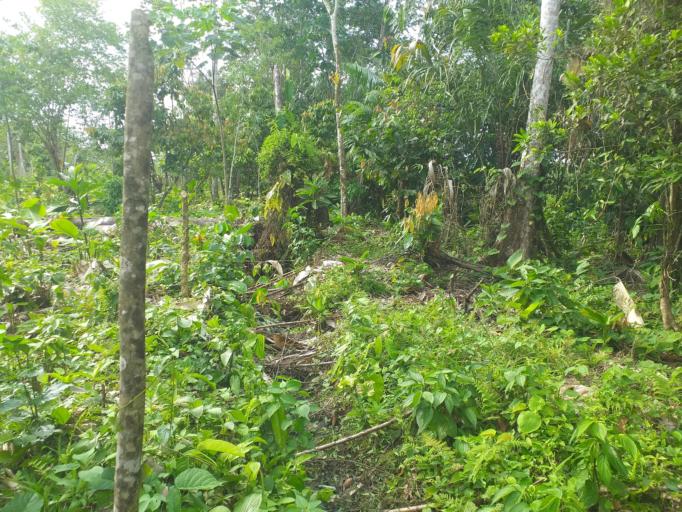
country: CO
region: Narino
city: La Tola
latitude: 2.3388
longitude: -78.3233
